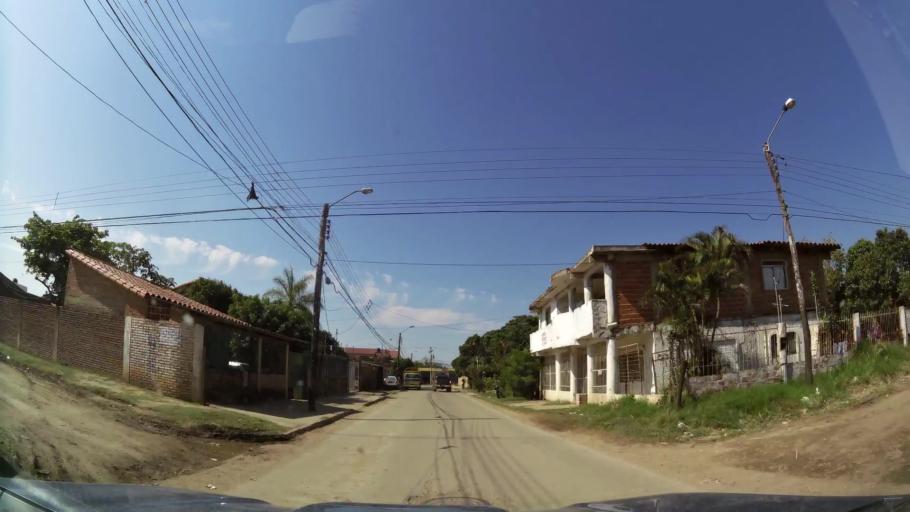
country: BO
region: Santa Cruz
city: Santa Cruz de la Sierra
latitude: -17.7588
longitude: -63.1172
